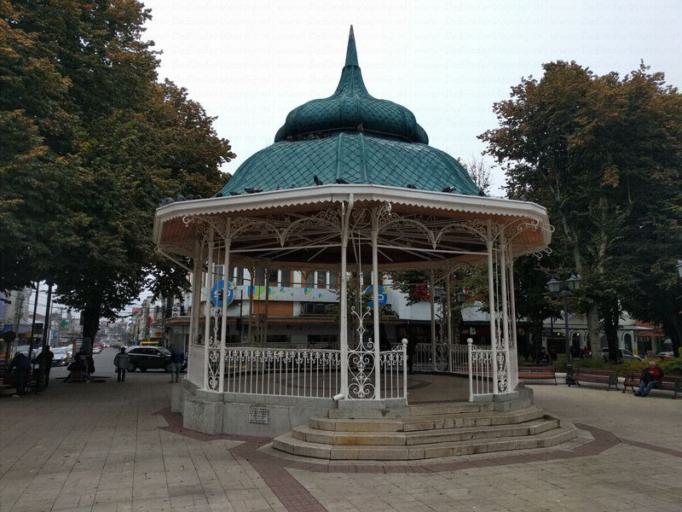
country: CL
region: Los Rios
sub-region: Provincia de Valdivia
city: Valdivia
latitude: -39.8141
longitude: -73.2460
